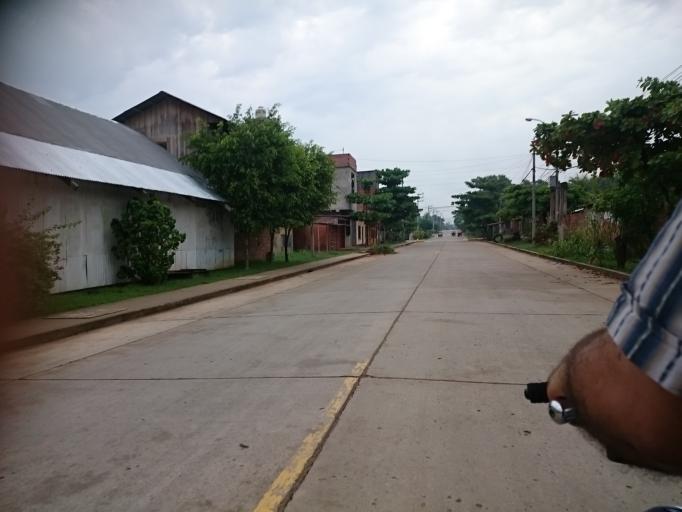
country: PE
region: Ucayali
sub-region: Provincia de Coronel Portillo
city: Puerto Callao
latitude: -8.3601
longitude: -74.5726
